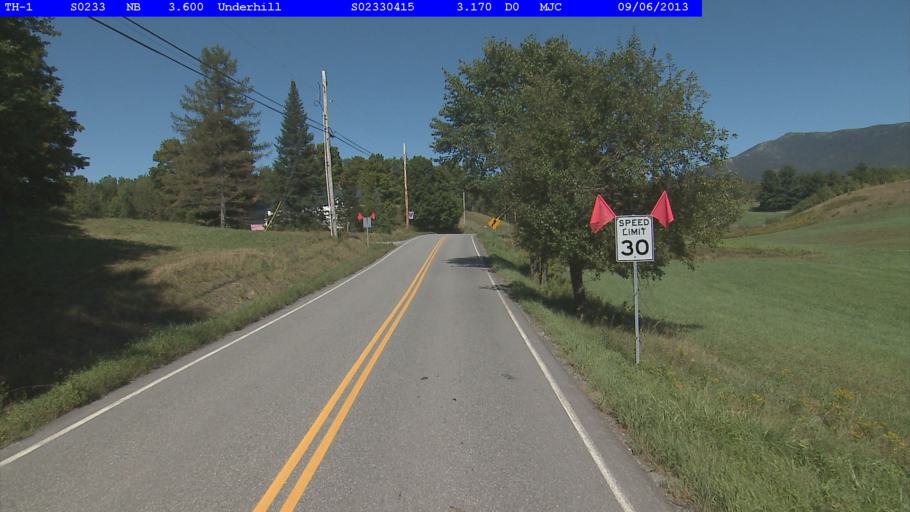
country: US
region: Vermont
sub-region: Chittenden County
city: Jericho
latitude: 44.5139
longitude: -72.8865
